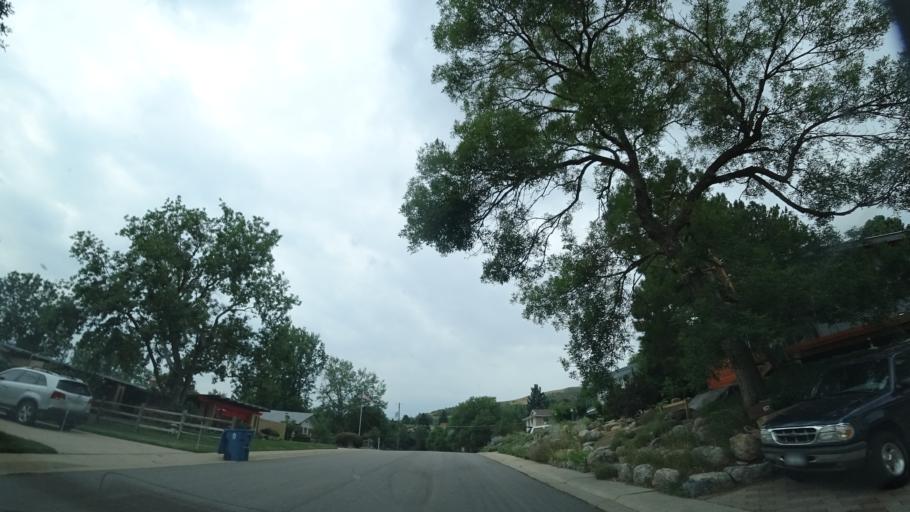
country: US
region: Colorado
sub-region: Jefferson County
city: West Pleasant View
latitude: 39.6990
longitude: -105.1517
